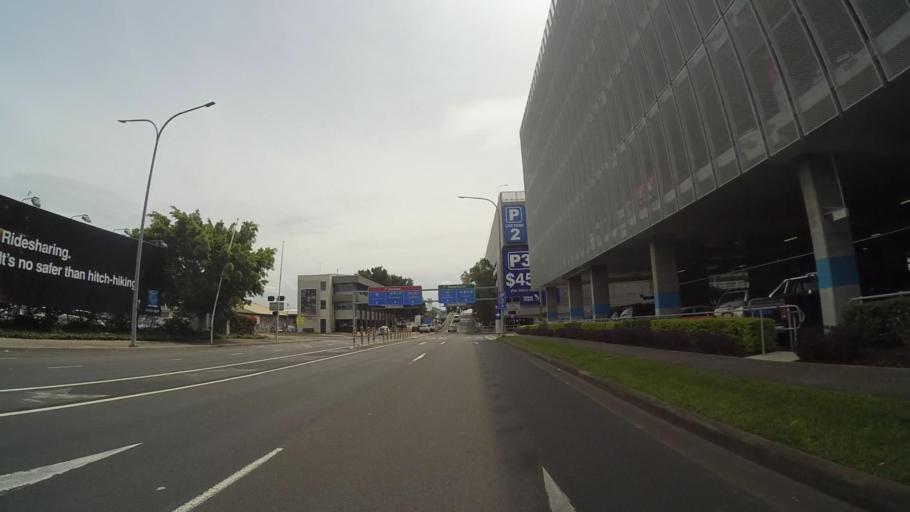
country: AU
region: New South Wales
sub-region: Botany Bay
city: Mascot
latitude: -33.9343
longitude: 151.1838
